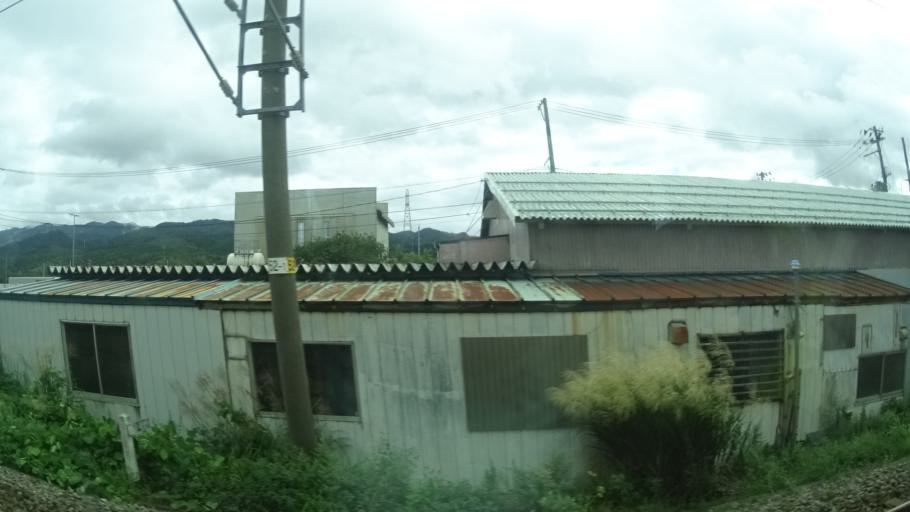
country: JP
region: Niigata
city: Shibata
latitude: 38.0018
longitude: 139.3707
